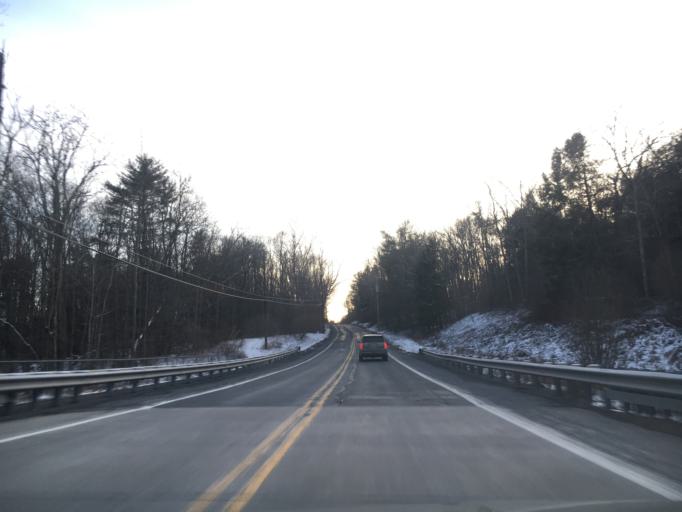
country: US
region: Pennsylvania
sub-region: Pike County
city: Saw Creek
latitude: 41.1109
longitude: -75.0954
